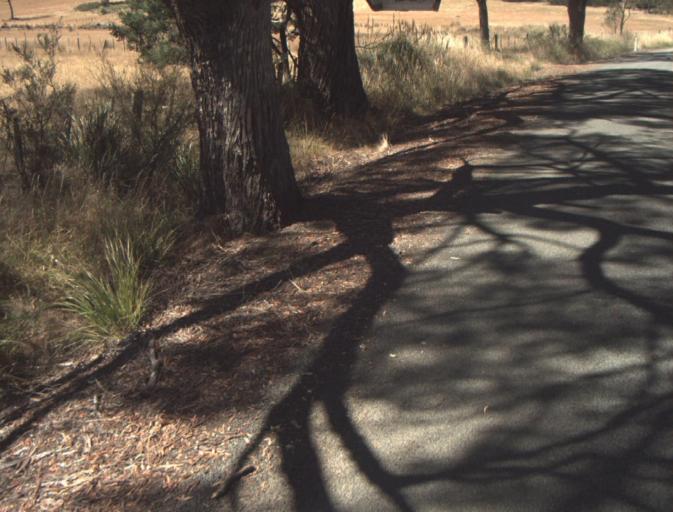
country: AU
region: Tasmania
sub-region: Launceston
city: Newstead
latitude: -41.3923
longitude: 147.3036
